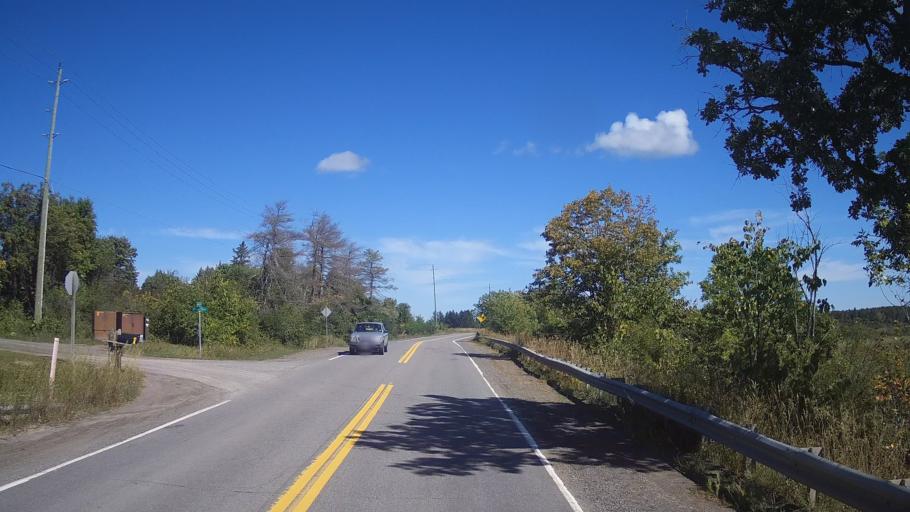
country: CA
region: Ontario
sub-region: Lanark County
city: Smiths Falls
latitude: 44.9668
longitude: -75.8249
